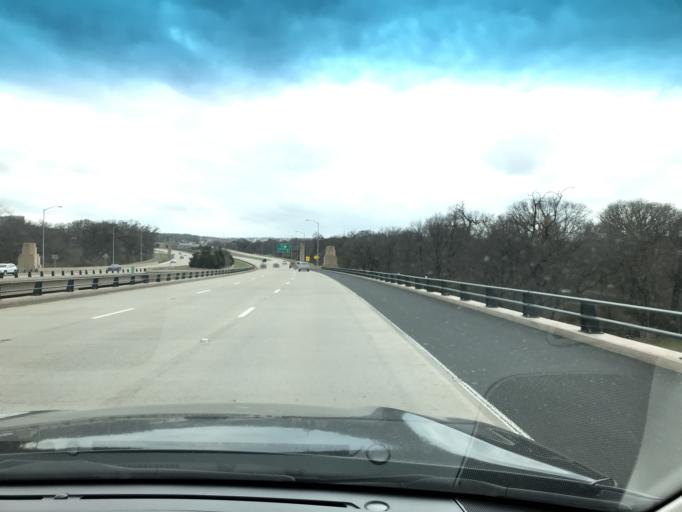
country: US
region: Texas
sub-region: Tarrant County
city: Westworth
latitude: 32.7063
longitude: -97.4055
